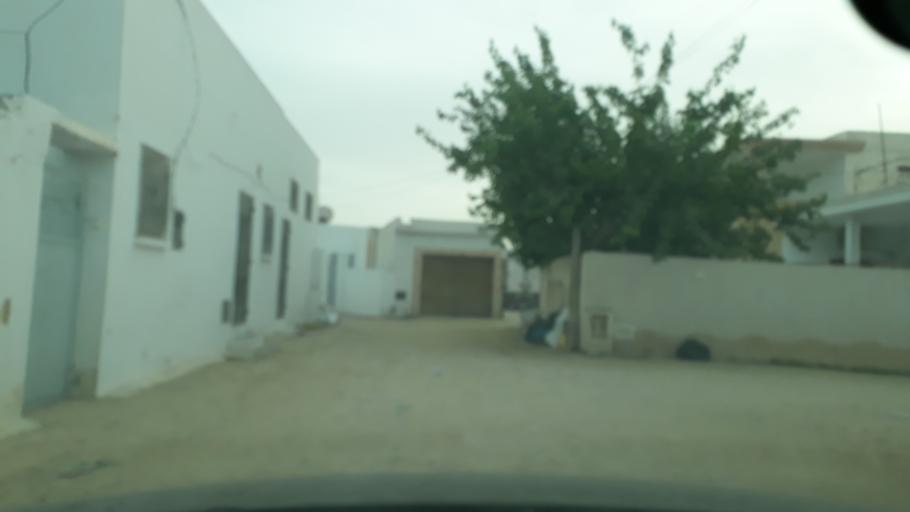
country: TN
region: Safaqis
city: Al Qarmadah
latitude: 34.8131
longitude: 10.7599
